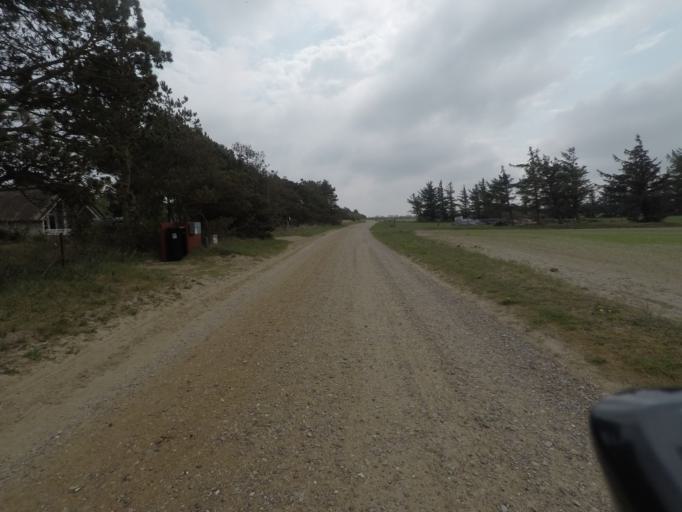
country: DE
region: Schleswig-Holstein
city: List
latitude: 55.0909
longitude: 8.5216
